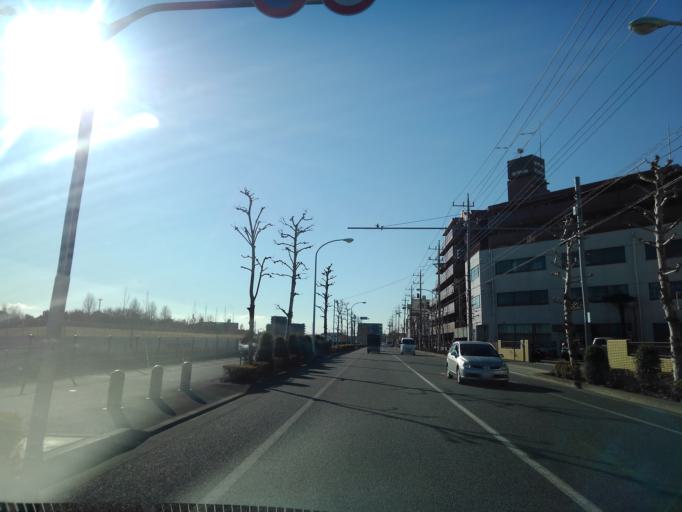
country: JP
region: Tokyo
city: Fussa
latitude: 35.7346
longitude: 139.3830
